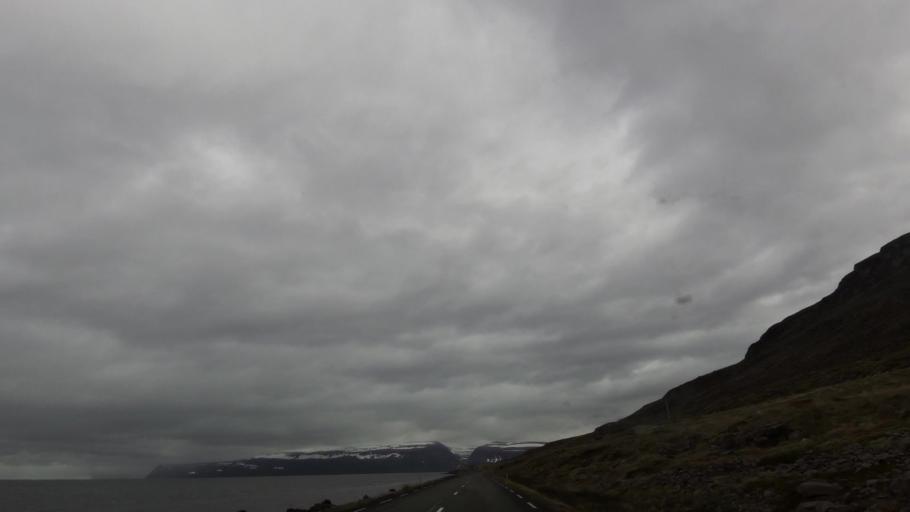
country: IS
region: Westfjords
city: Isafjoerdur
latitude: 66.0337
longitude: -22.7741
